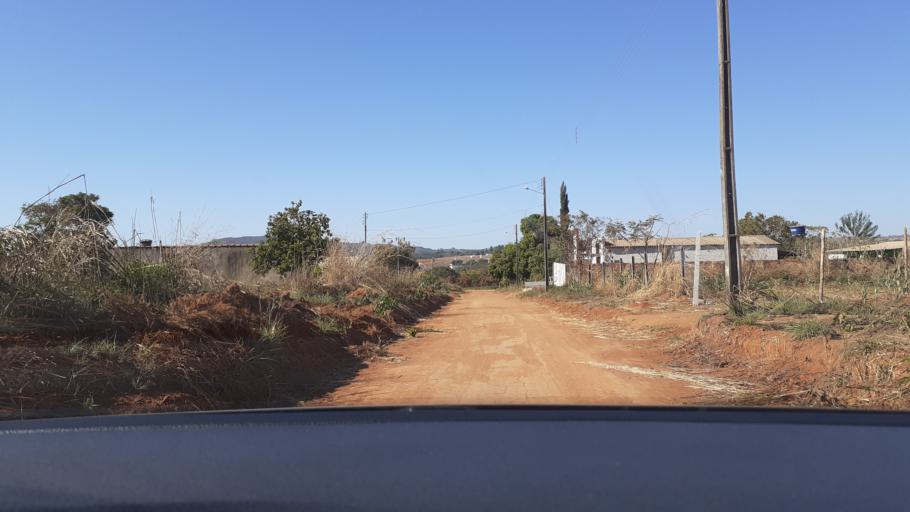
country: BR
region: Goias
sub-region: Aparecida De Goiania
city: Aparecida de Goiania
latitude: -16.8656
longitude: -49.2569
